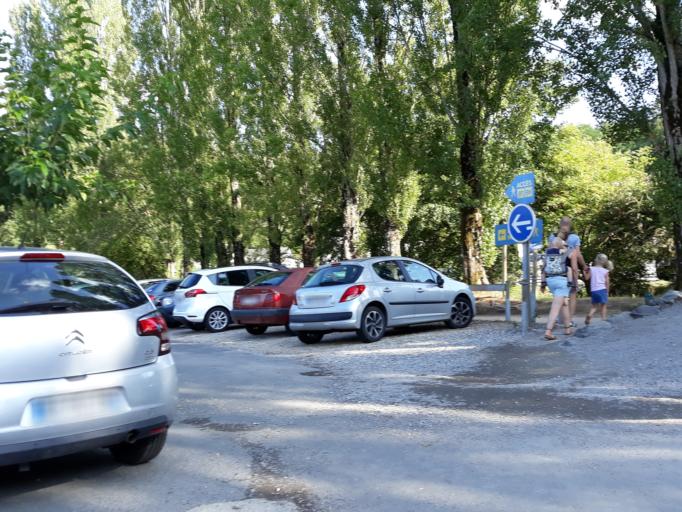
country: FR
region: Centre
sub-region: Departement du Loir-et-Cher
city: Saint-Aignan
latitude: 47.2472
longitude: 1.3539
